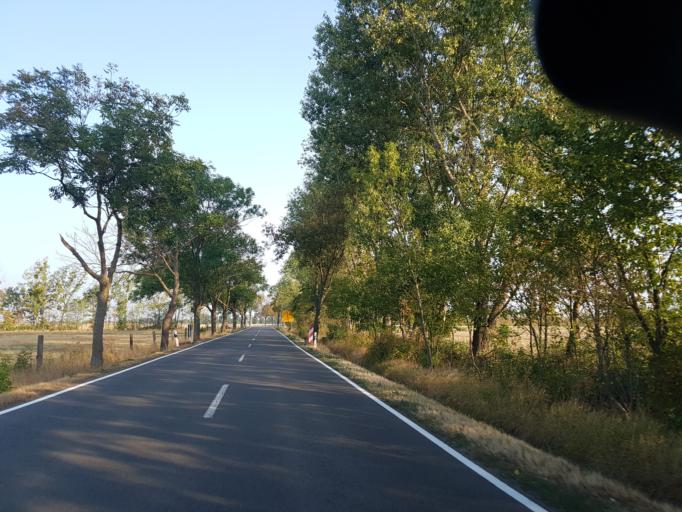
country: DE
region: Saxony-Anhalt
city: Muhlanger
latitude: 51.7856
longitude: 12.7108
